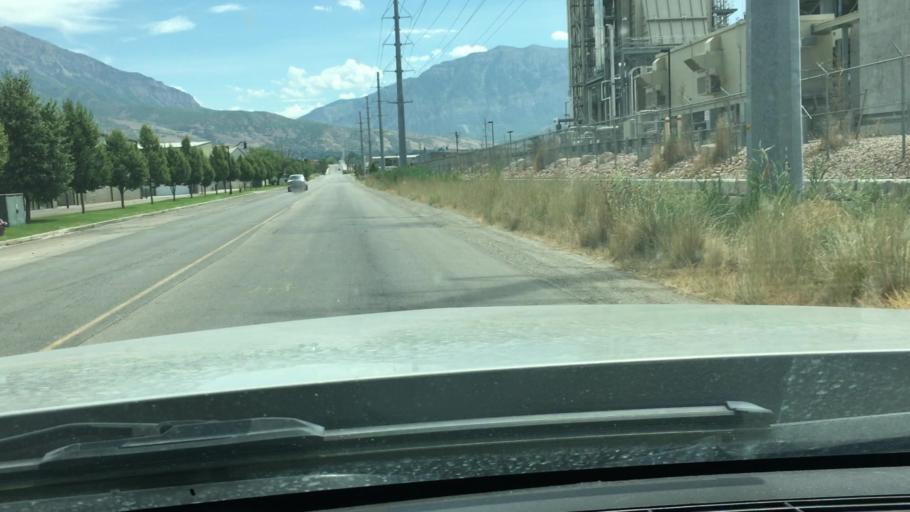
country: US
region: Utah
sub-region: Utah County
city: Pleasant Grove
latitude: 40.3334
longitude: -111.7563
